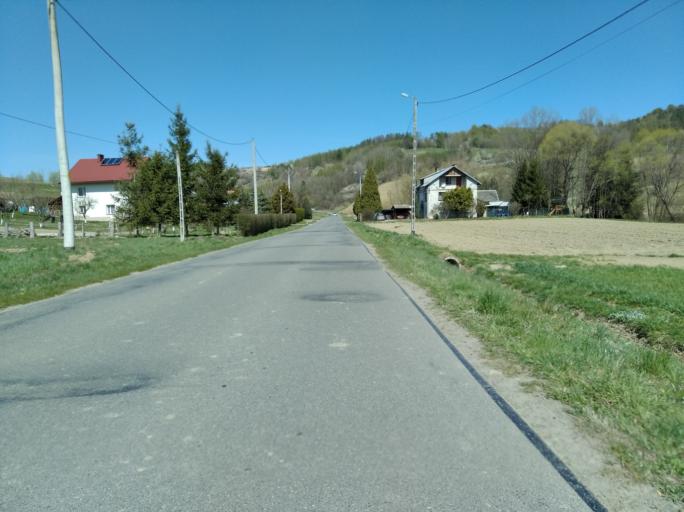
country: PL
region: Subcarpathian Voivodeship
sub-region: Powiat brzozowski
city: Dydnia
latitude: 49.7000
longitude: 22.1523
